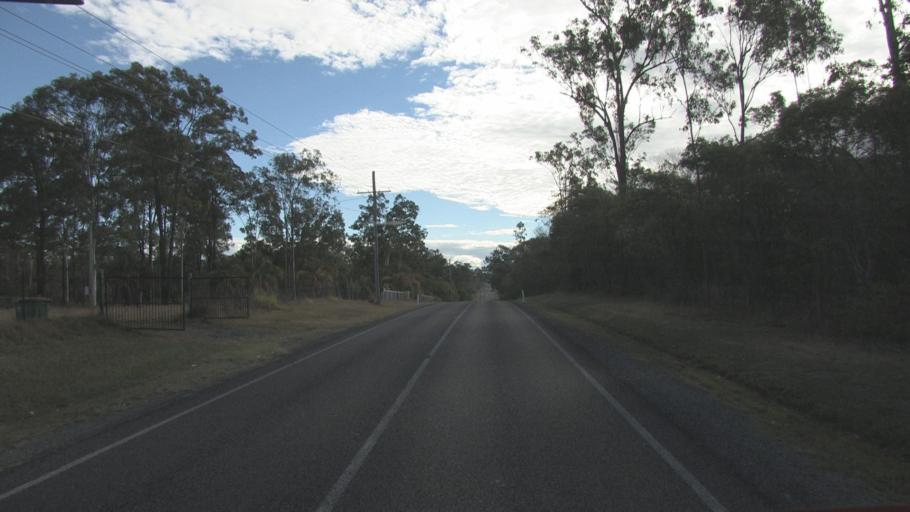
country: AU
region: Queensland
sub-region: Logan
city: Cedar Vale
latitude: -27.8354
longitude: 153.0425
